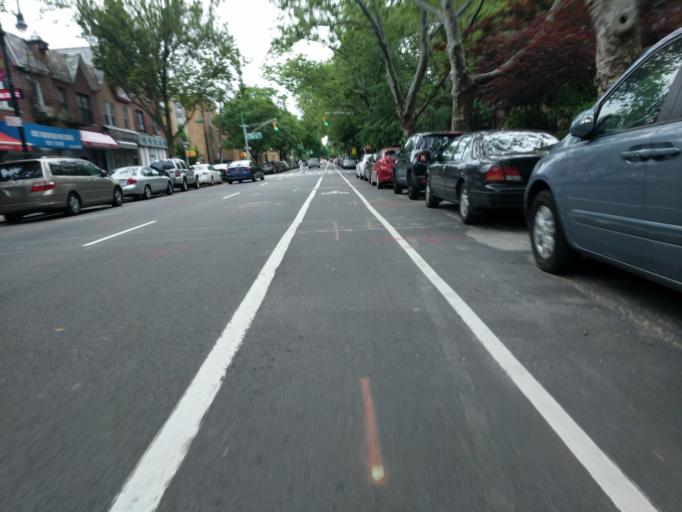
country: US
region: New York
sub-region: Queens County
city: Long Island City
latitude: 40.7466
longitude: -73.9180
